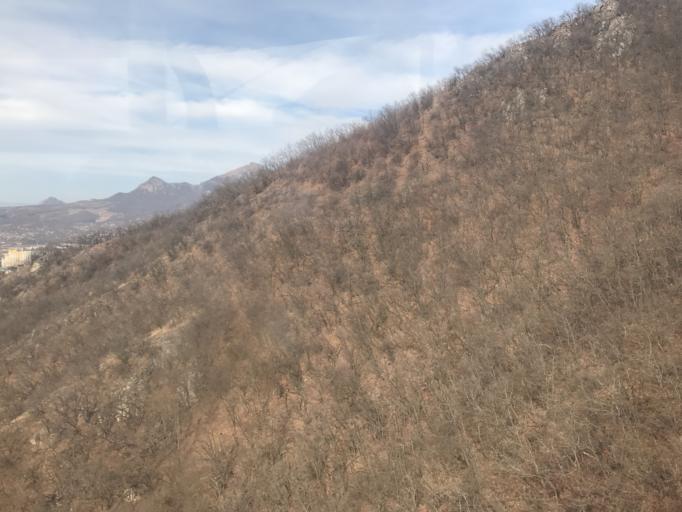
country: RU
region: Stavropol'skiy
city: Goryachevodskiy
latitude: 44.0471
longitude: 43.0855
